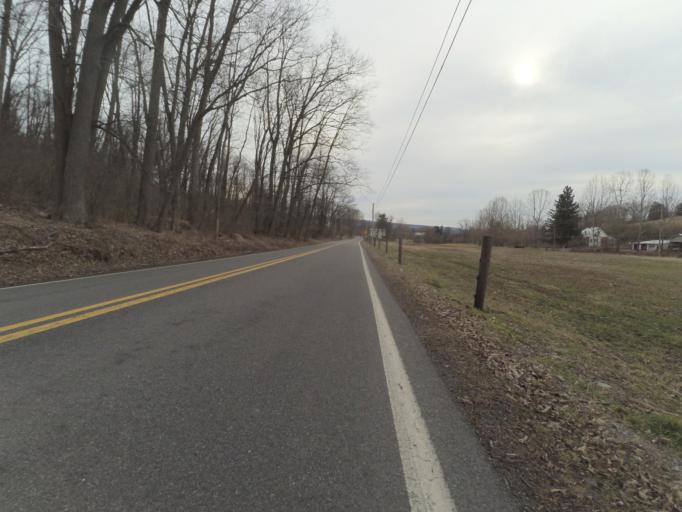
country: US
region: Pennsylvania
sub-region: Centre County
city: State College
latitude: 40.7787
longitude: -77.8307
